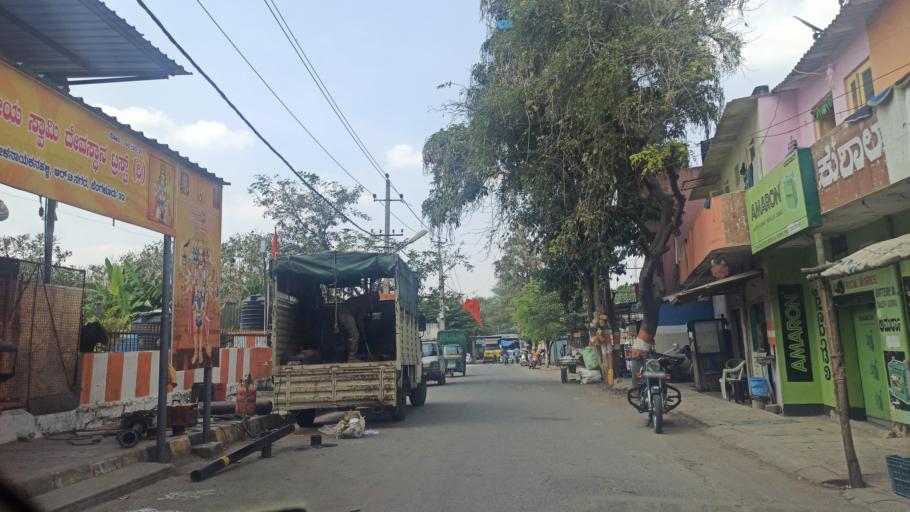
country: IN
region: Karnataka
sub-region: Bangalore Urban
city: Yelahanka
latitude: 13.0381
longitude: 77.5965
